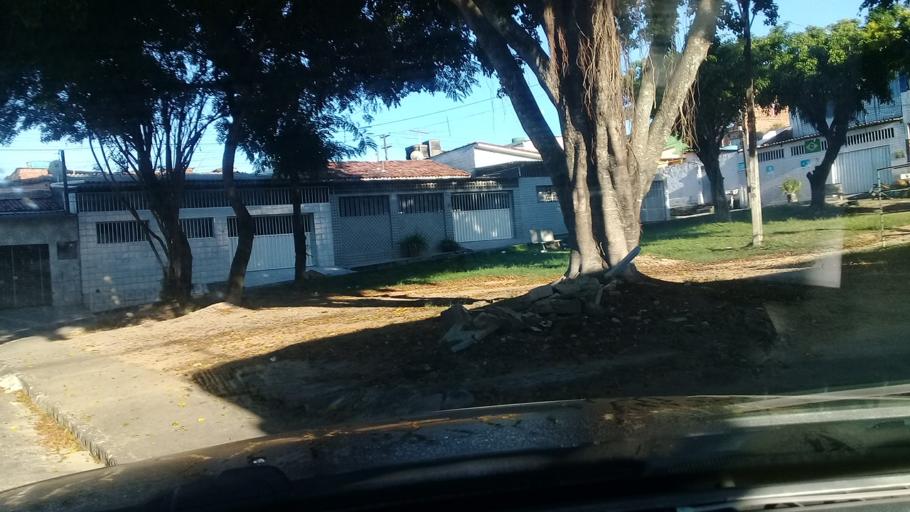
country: BR
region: Pernambuco
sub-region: Jaboatao Dos Guararapes
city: Jaboatao dos Guararapes
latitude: -8.1169
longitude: -34.9545
